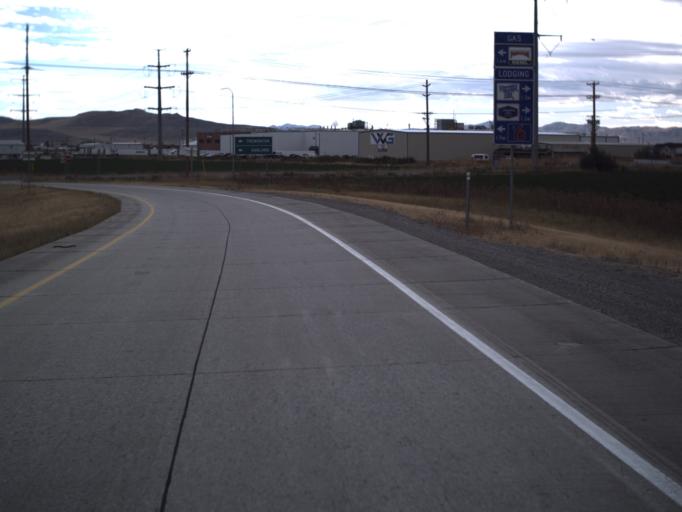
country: US
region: Utah
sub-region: Box Elder County
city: Tremonton
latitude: 41.7273
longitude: -112.1938
